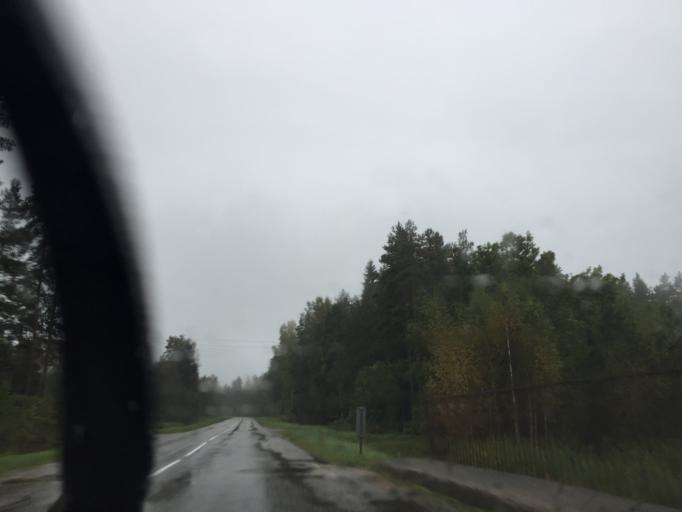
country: LV
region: Incukalns
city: Incukalns
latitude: 57.0291
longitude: 24.6825
